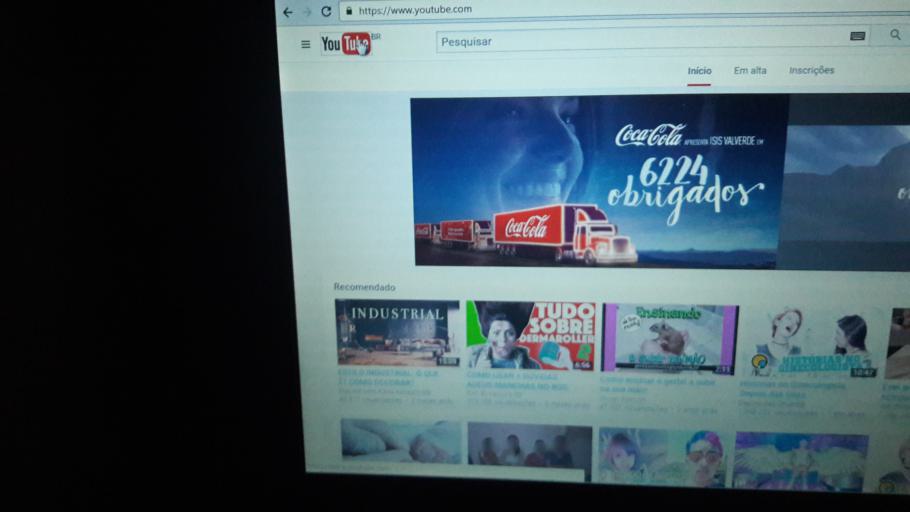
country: BR
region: Minas Gerais
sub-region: Belo Horizonte
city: Belo Horizonte
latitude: -19.9392
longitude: -43.9134
